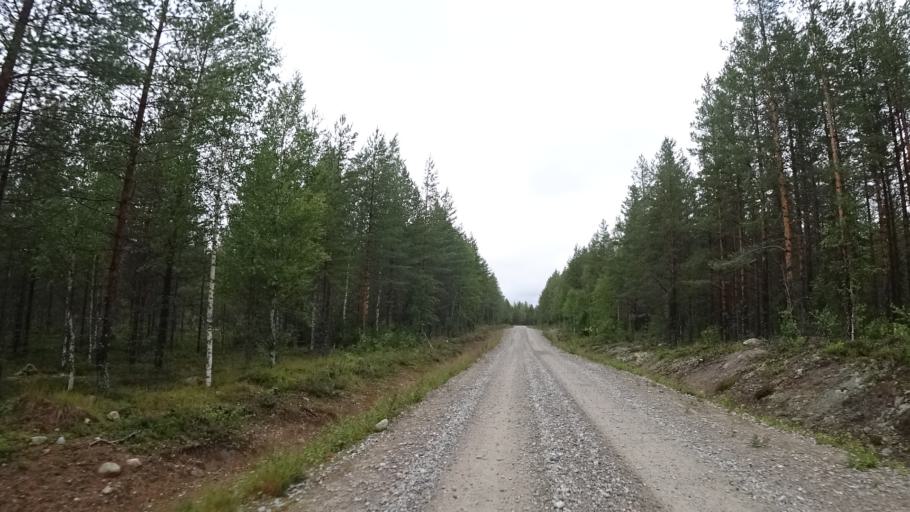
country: FI
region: North Karelia
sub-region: Pielisen Karjala
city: Lieksa
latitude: 63.4684
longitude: 30.2826
